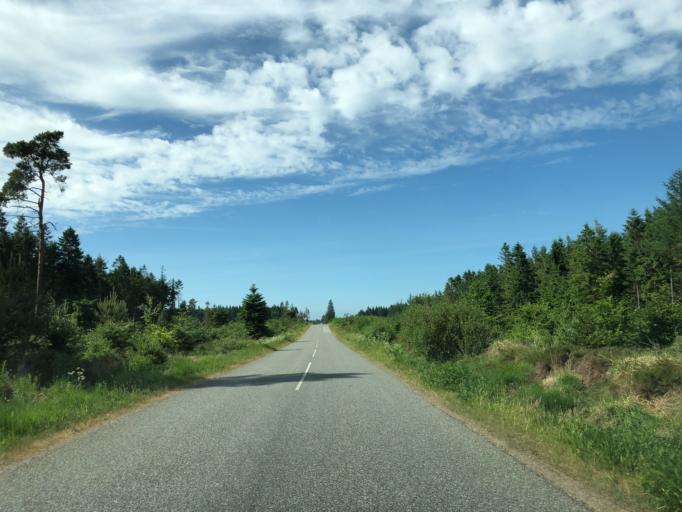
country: DK
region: Central Jutland
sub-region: Herning Kommune
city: Lind
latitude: 56.0469
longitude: 8.9305
